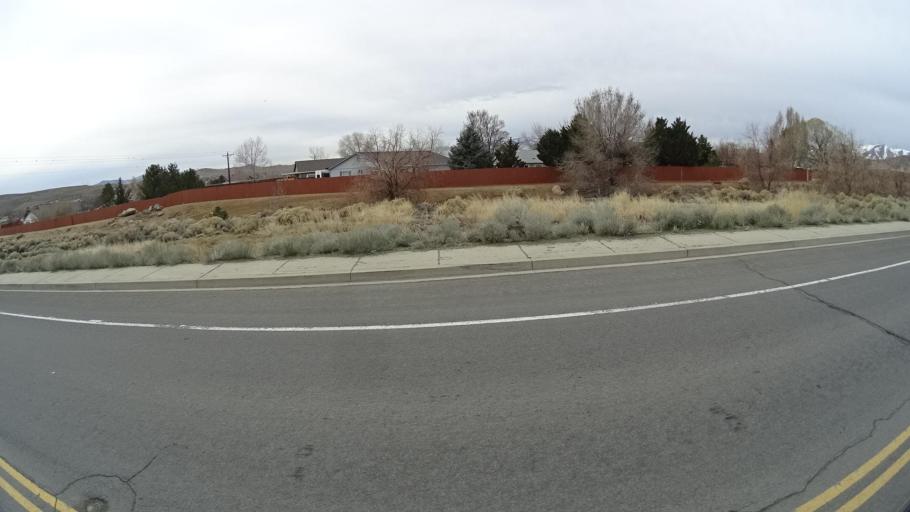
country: US
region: Nevada
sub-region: Washoe County
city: Sun Valley
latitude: 39.6138
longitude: -119.7634
